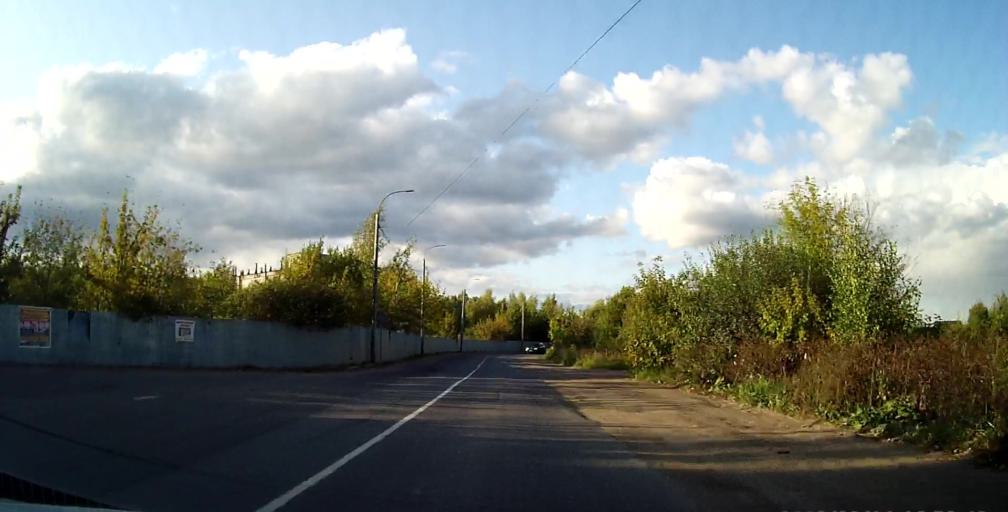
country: RU
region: Moskovskaya
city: Klimovsk
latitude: 55.3762
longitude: 37.5629
